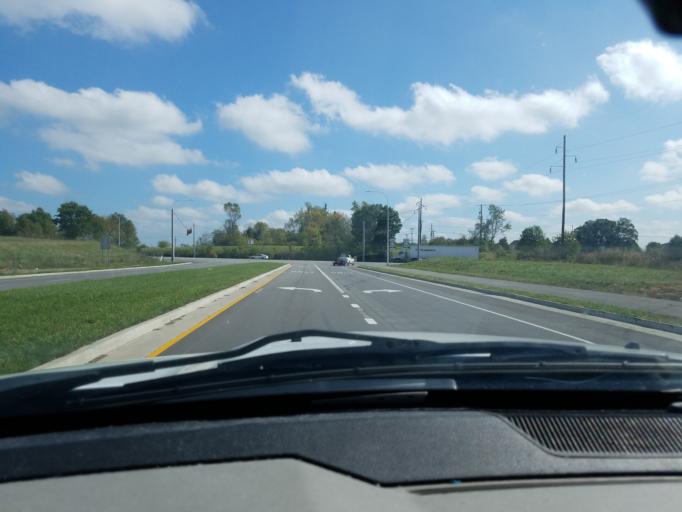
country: US
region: Kentucky
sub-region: Scott County
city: Georgetown
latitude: 38.2443
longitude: -84.5296
